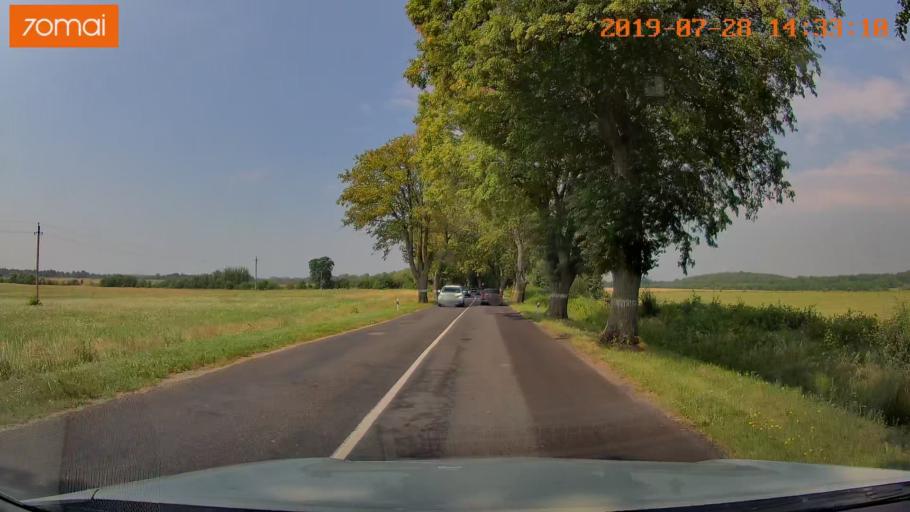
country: RU
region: Kaliningrad
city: Primorsk
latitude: 54.8177
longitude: 20.0343
